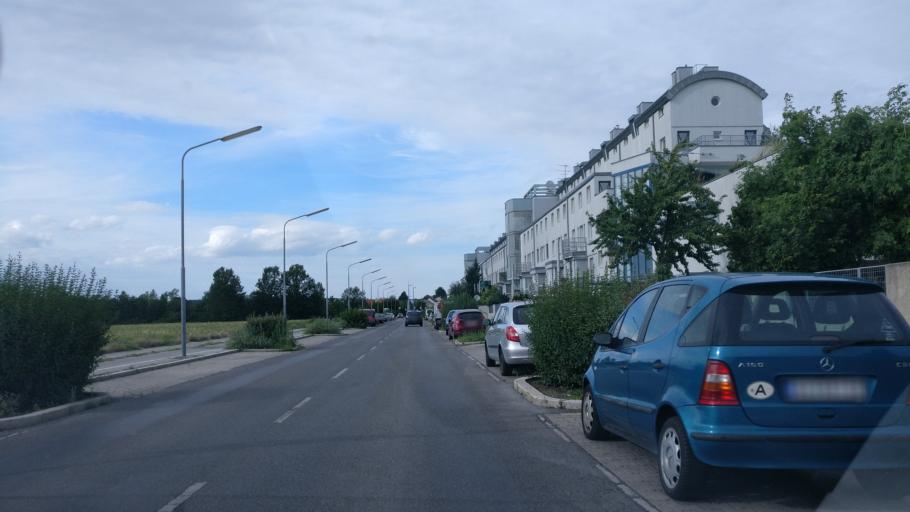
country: AT
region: Lower Austria
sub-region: Politischer Bezirk Korneuburg
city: Hagenbrunn
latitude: 48.2875
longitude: 16.4102
